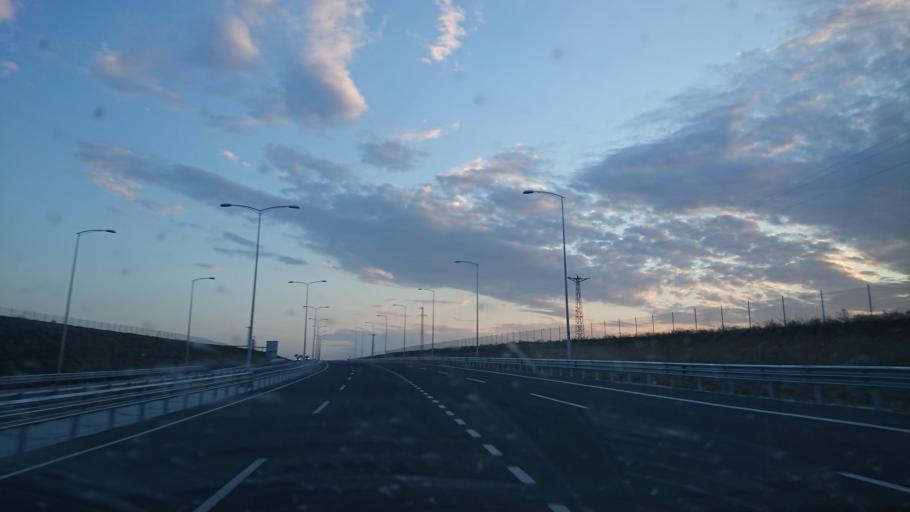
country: TR
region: Aksaray
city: Balci
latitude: 38.7698
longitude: 34.0999
